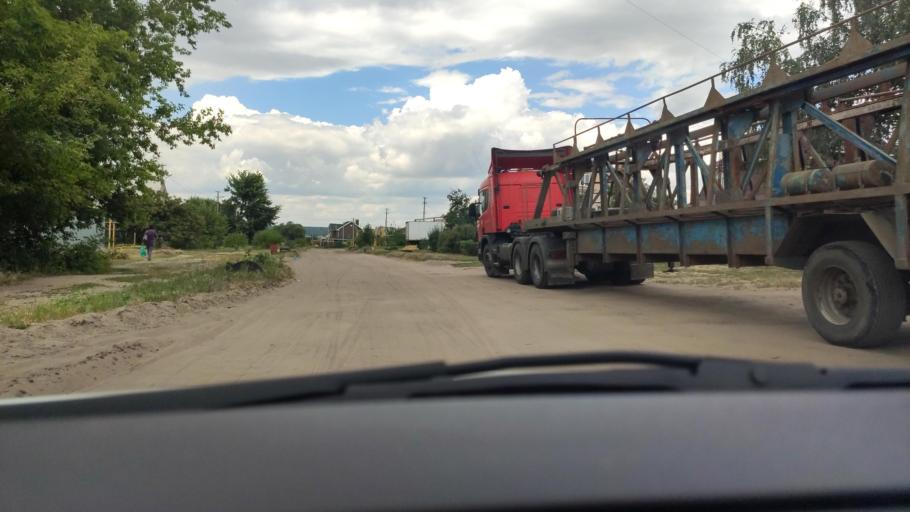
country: RU
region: Voronezj
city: Pridonskoy
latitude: 51.6978
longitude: 39.0886
